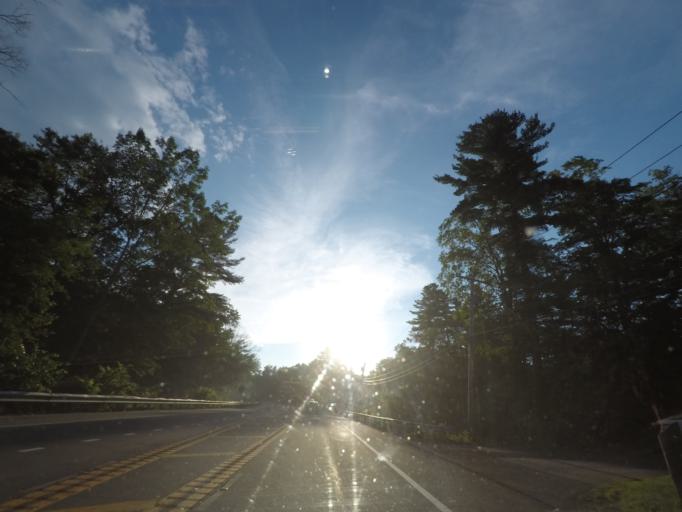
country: US
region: Massachusetts
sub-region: Worcester County
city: Fiskdale
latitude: 42.1136
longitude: -72.1536
